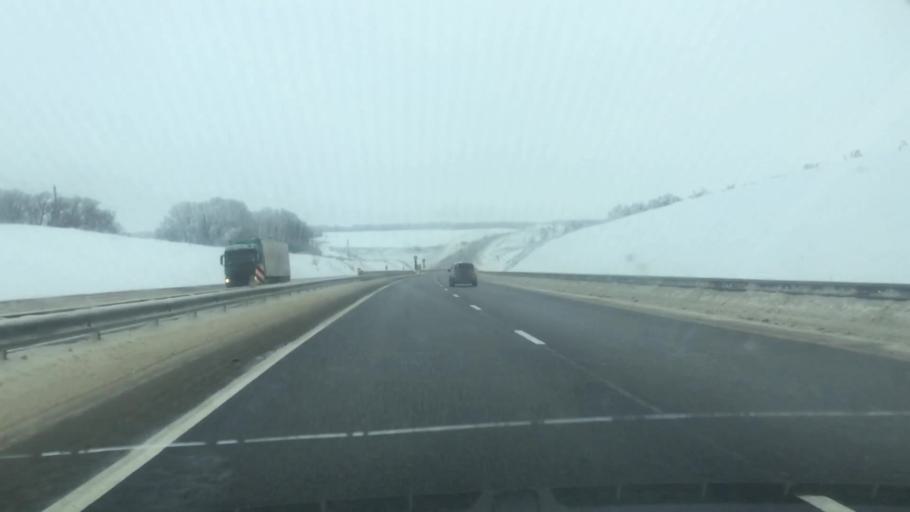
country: RU
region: Lipetsk
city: Stanovoye
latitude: 52.8720
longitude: 38.2795
